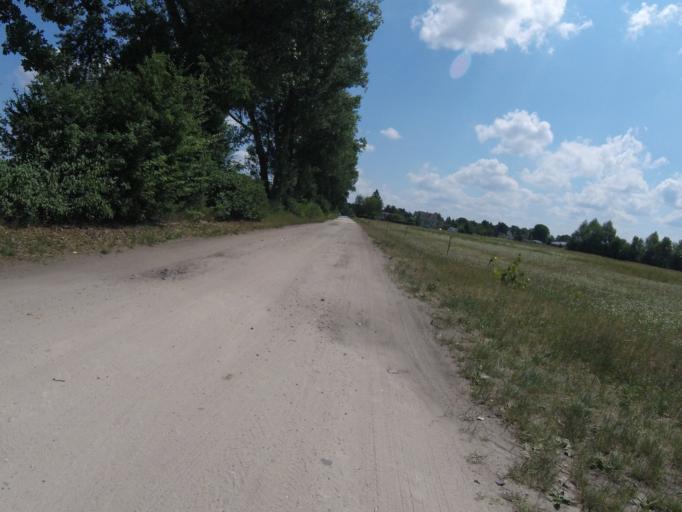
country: DE
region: Brandenburg
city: Bestensee
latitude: 52.2592
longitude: 13.7265
